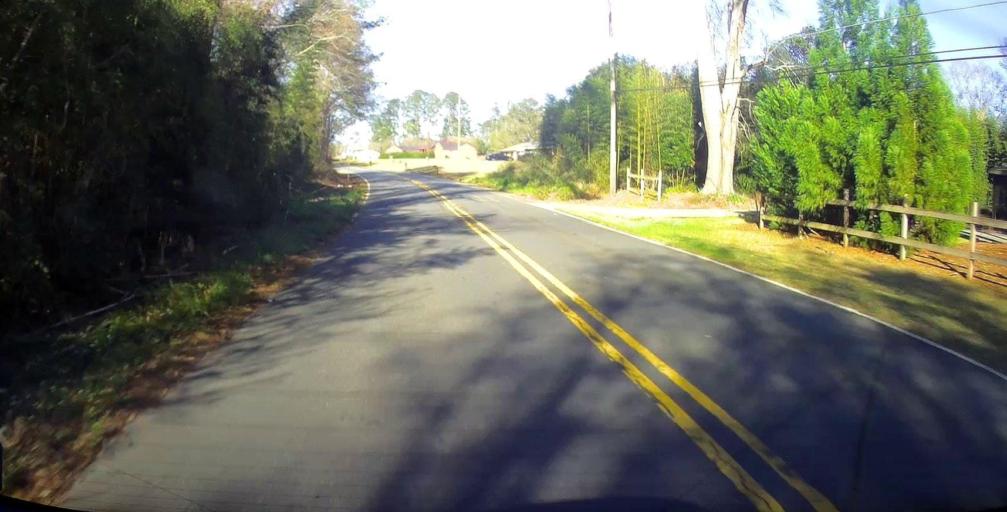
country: US
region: Georgia
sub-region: Peach County
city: Fort Valley
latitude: 32.5262
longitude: -83.9081
